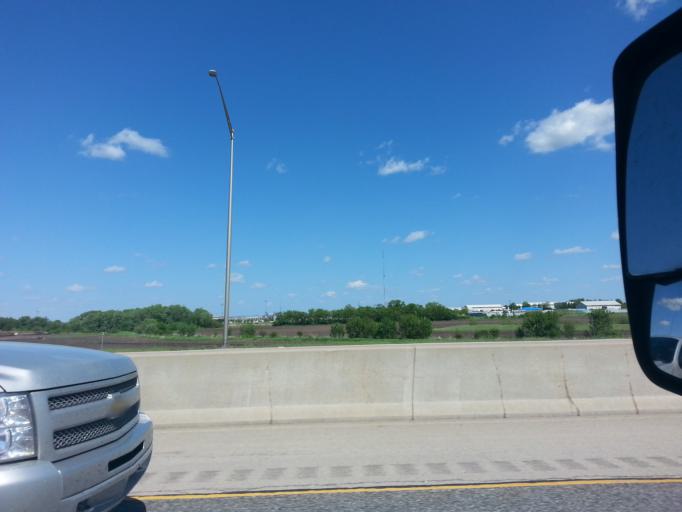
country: US
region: Illinois
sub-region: Winnebago County
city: Machesney Park
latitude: 42.3234
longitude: -88.9646
